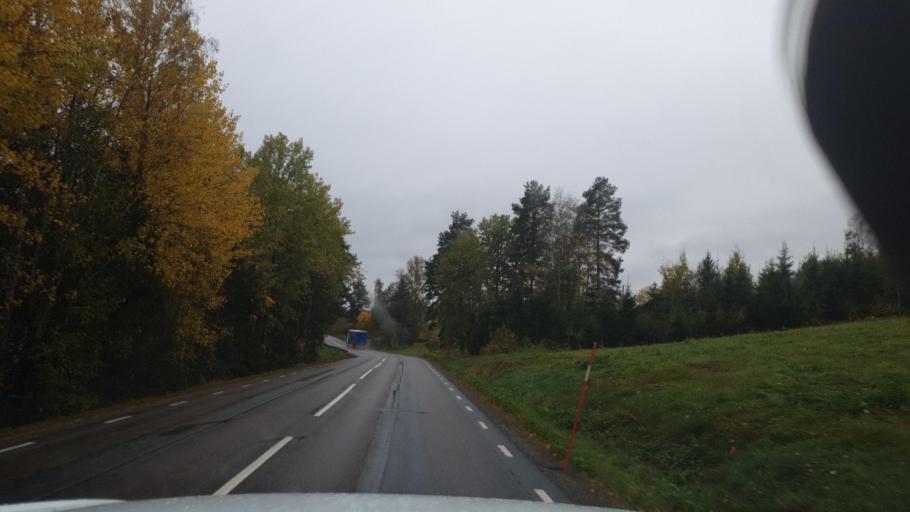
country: SE
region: Vaermland
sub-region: Eda Kommun
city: Charlottenberg
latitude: 59.8159
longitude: 12.2589
